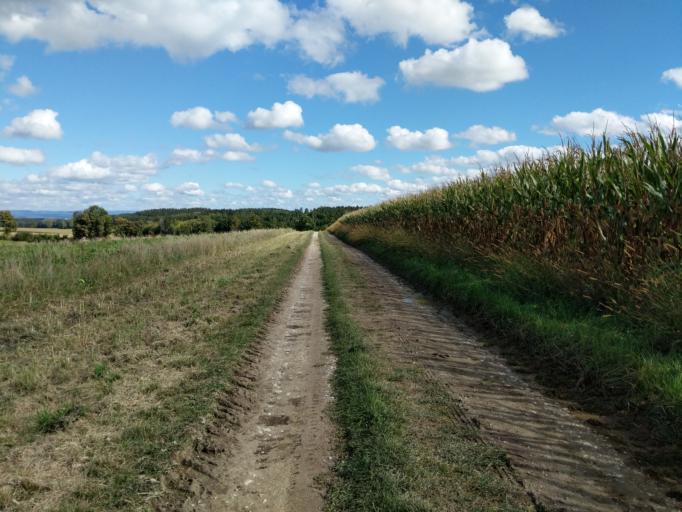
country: DE
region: Bavaria
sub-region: Lower Bavaria
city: Bad Abbach
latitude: 48.9466
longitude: 12.0561
